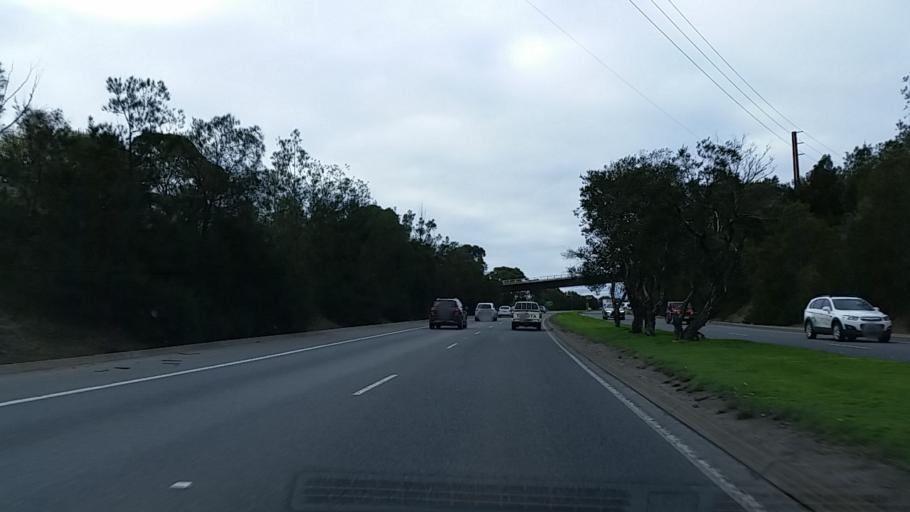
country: AU
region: South Australia
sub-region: Onkaparinga
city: Noarlunga
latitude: -35.1730
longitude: 138.5004
